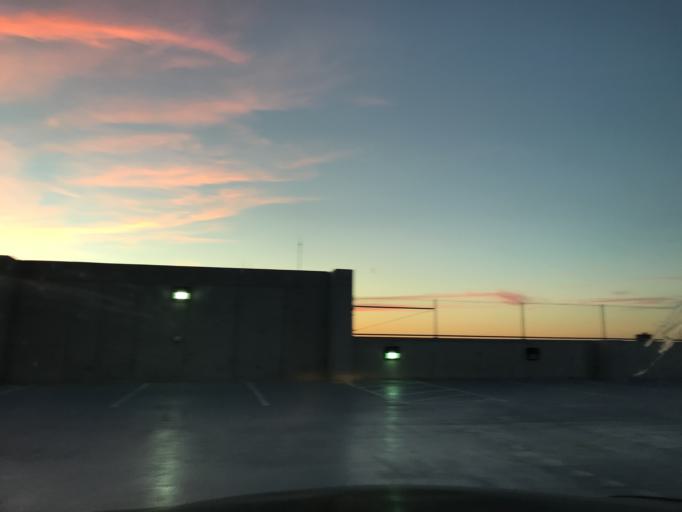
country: US
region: Maryland
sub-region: City of Baltimore
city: Baltimore
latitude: 39.3348
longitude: -76.6298
